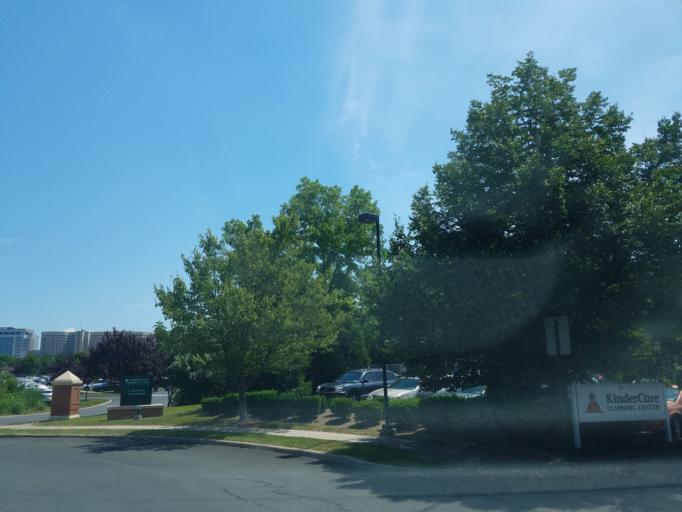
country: US
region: Connecticut
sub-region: Hartford County
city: Farmington
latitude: 41.7268
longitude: -72.8007
